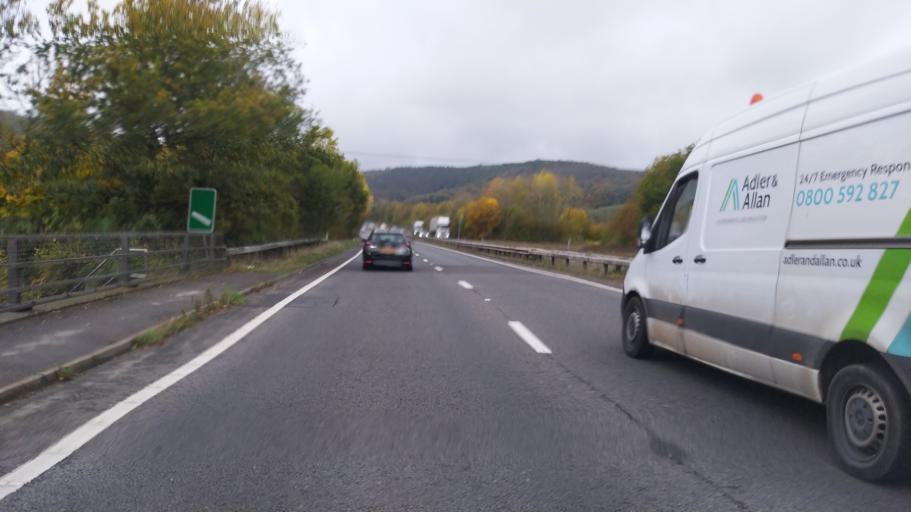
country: GB
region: England
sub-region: Hampshire
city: Petersfield
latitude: 50.9852
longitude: -0.9618
